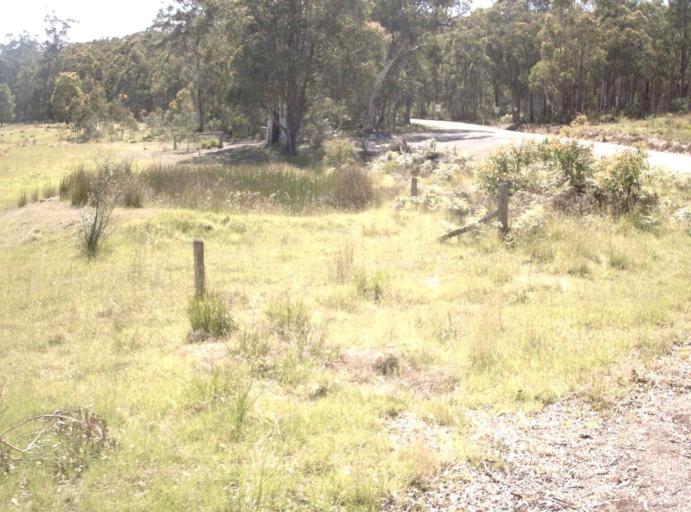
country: AU
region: New South Wales
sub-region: Bombala
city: Bombala
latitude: -37.1425
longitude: 148.7260
